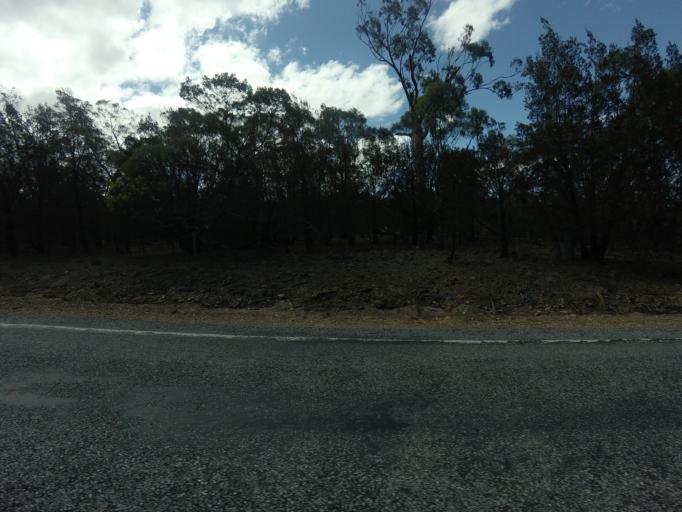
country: AU
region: Tasmania
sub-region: Break O'Day
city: St Helens
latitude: -42.0164
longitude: 148.0019
